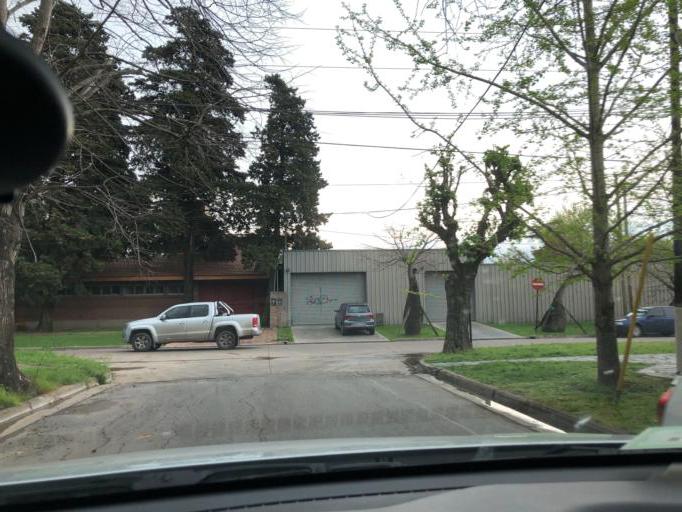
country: AR
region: Buenos Aires
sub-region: Partido de La Plata
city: La Plata
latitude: -34.8763
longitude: -58.0462
